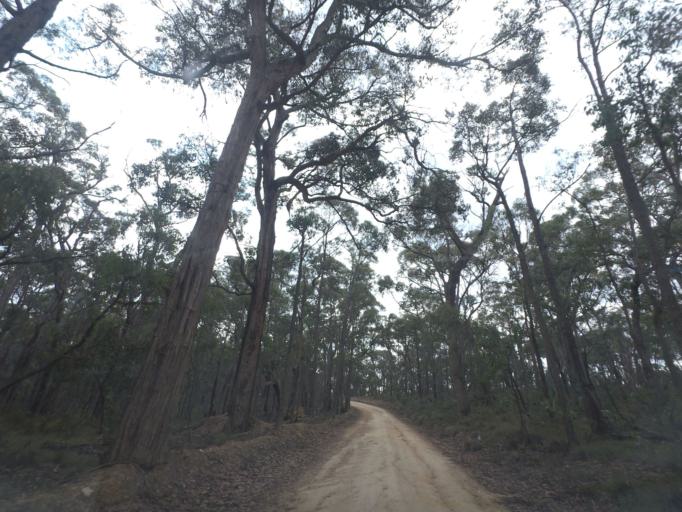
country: AU
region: Victoria
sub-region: Moorabool
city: Bacchus Marsh
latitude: -37.5130
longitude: 144.4335
